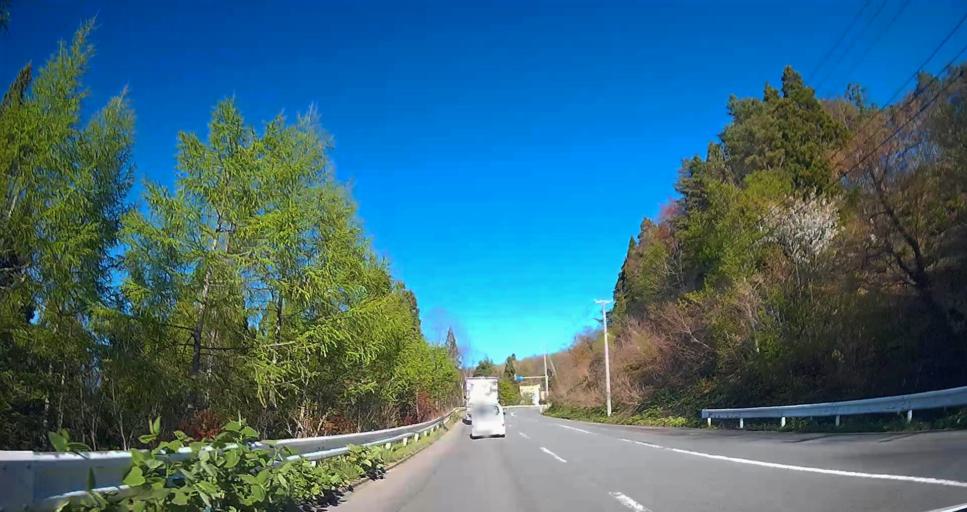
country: JP
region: Aomori
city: Mutsu
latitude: 41.4330
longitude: 141.1341
